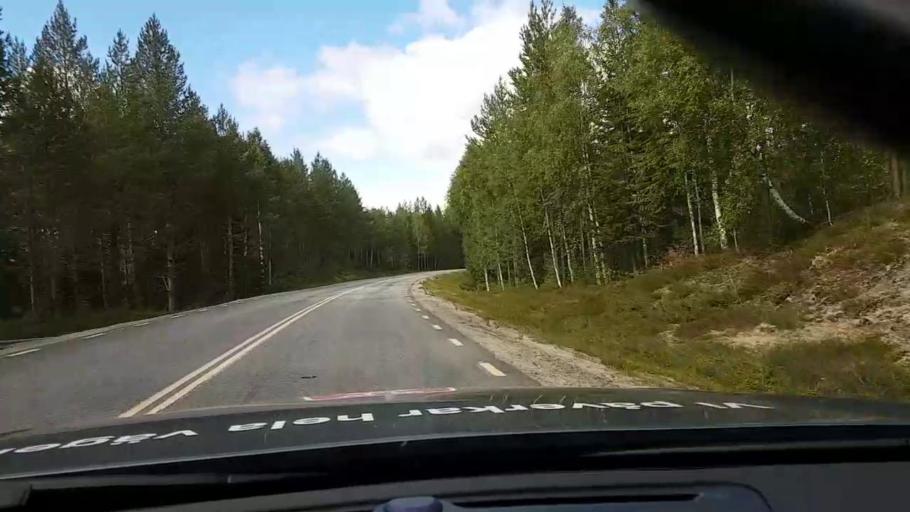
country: SE
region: Vaesternorrland
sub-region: OErnskoeldsviks Kommun
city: Bredbyn
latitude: 63.5310
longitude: 17.9706
